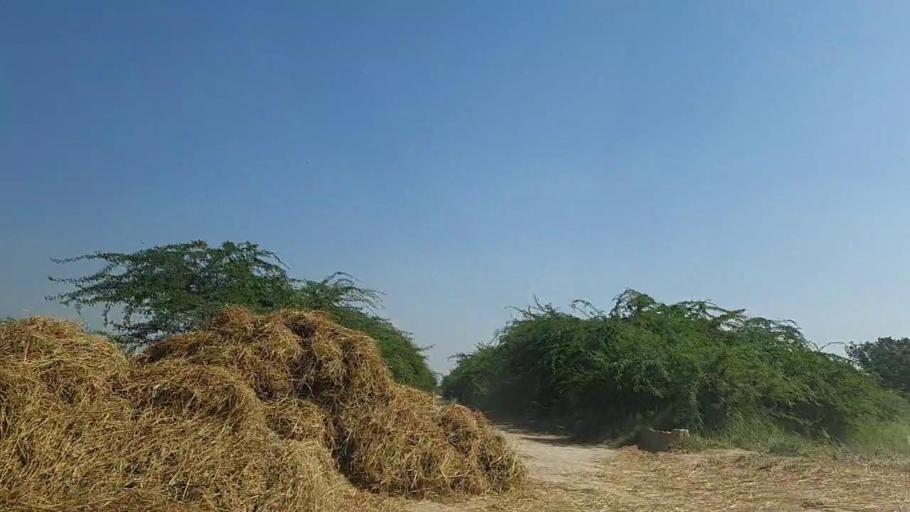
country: PK
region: Sindh
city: Mirpur Batoro
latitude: 24.7312
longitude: 68.2152
